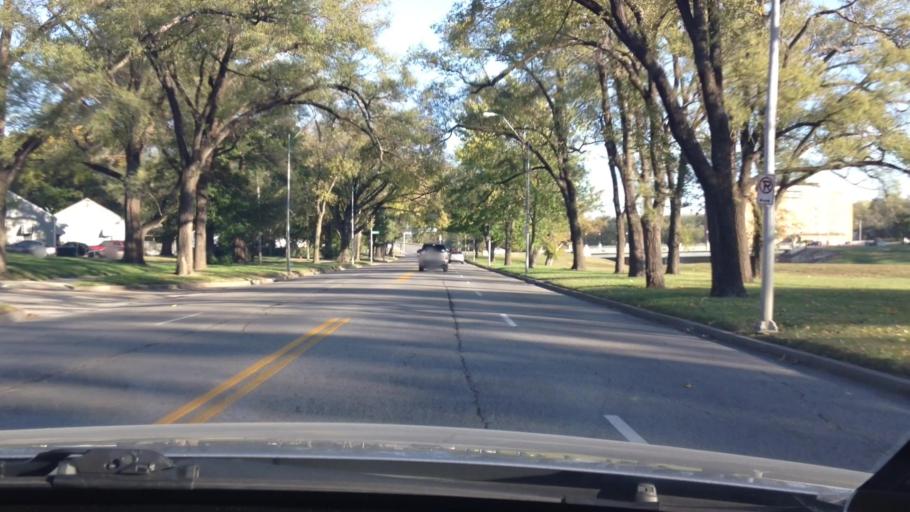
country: US
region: Kansas
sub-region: Johnson County
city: Westwood
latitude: 39.0419
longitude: -94.5570
